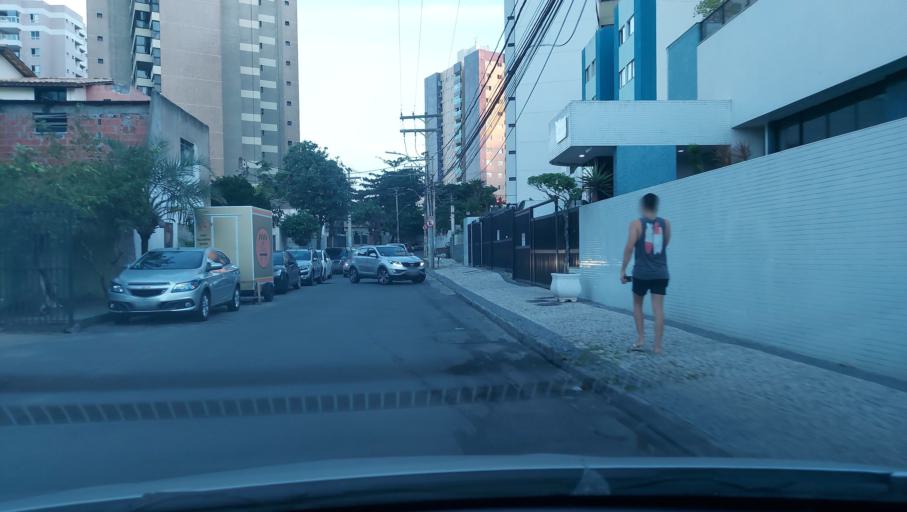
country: BR
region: Bahia
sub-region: Salvador
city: Salvador
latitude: -12.9862
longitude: -38.4392
